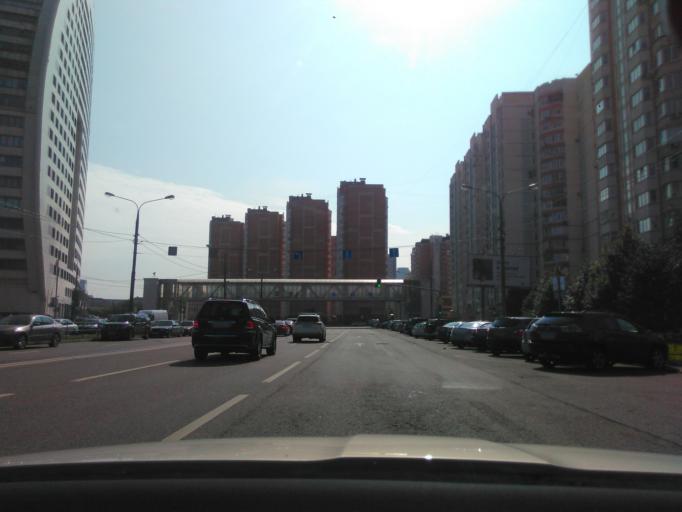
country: RU
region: Moscow
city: Sokol
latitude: 55.7823
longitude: 37.5286
